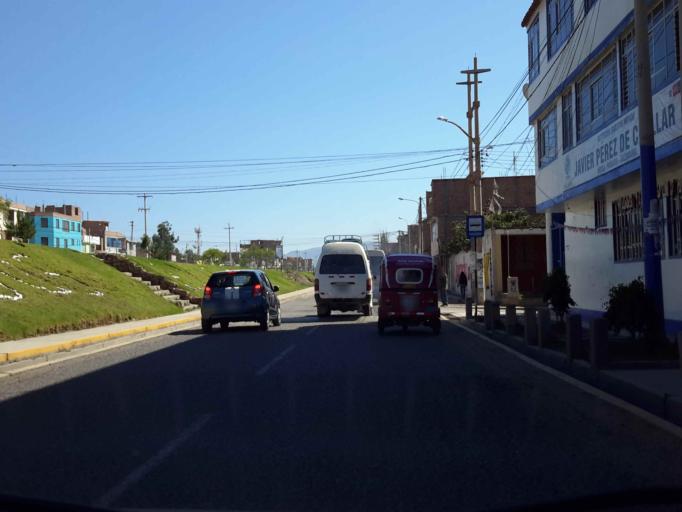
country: PE
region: Ayacucho
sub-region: Provincia de Huamanga
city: Ayacucho
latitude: -13.1410
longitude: -74.2285
